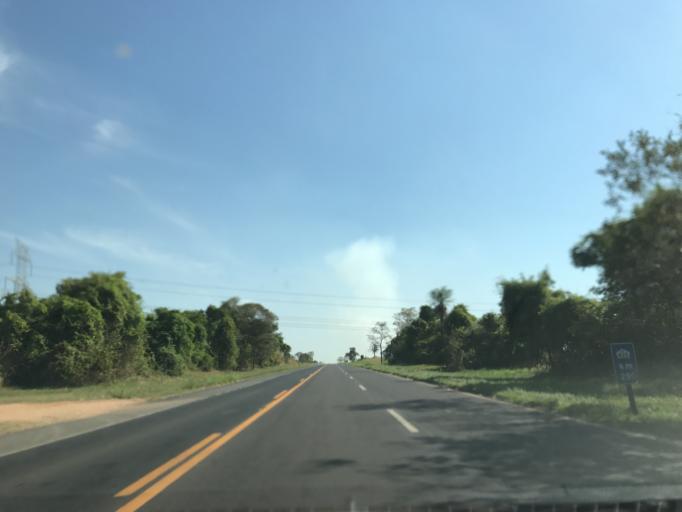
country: BR
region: Sao Paulo
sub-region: Penapolis
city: Penapolis
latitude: -21.3515
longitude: -50.0581
